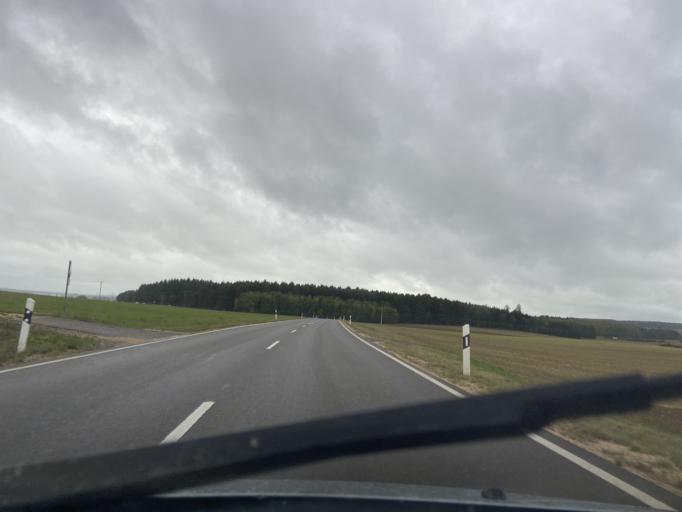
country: DE
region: Baden-Wuerttemberg
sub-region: Tuebingen Region
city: Messkirch
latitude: 48.0384
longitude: 9.1215
